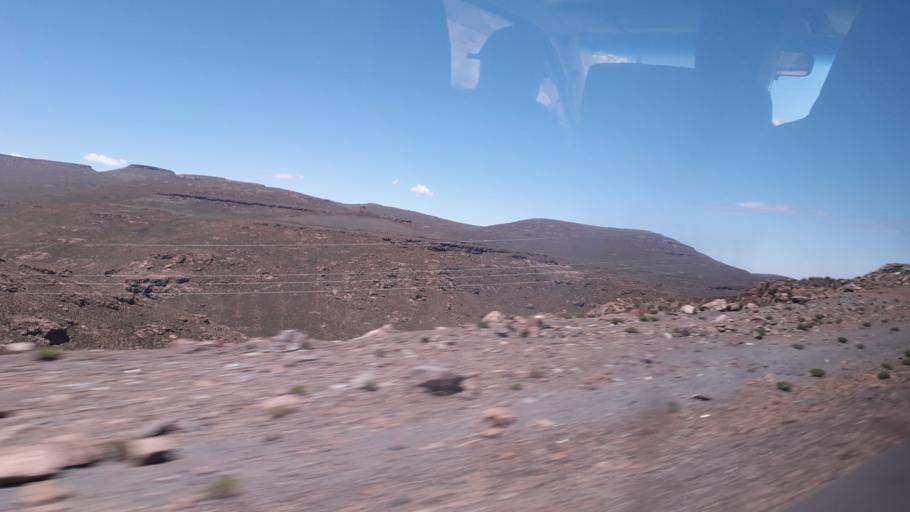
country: ZA
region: Orange Free State
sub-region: Thabo Mofutsanyana District Municipality
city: Phuthaditjhaba
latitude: -28.8294
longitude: 28.7348
